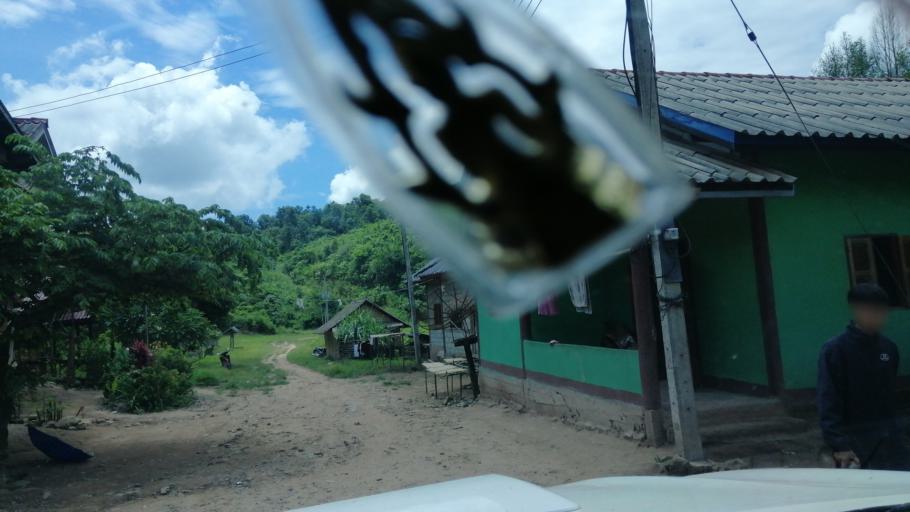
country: TH
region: Nan
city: Chaloem Phra Kiat
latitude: 19.7249
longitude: 101.4368
